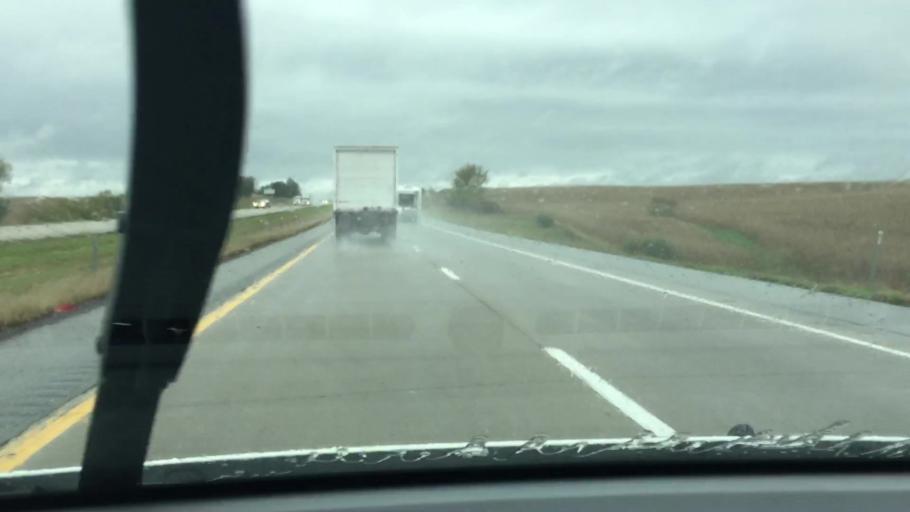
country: US
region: Iowa
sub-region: Poweshiek County
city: Brooklyn
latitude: 41.6961
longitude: -92.3864
